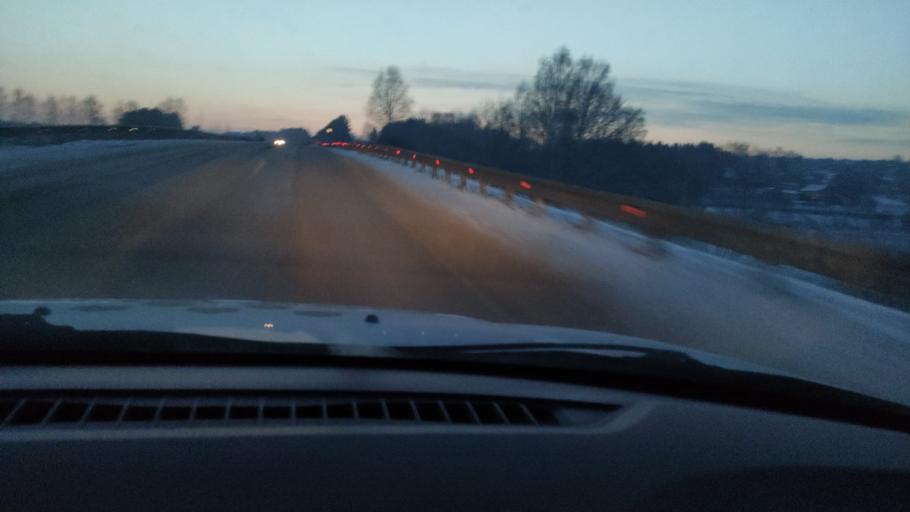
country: RU
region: Perm
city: Kungur
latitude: 57.4227
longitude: 56.9258
